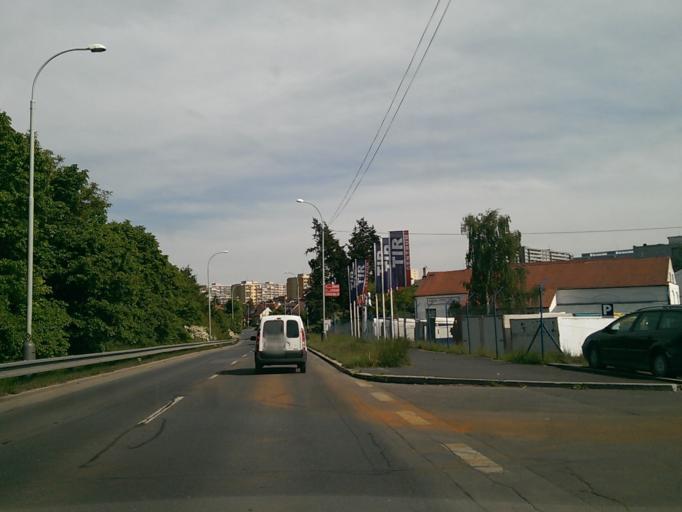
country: CZ
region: Central Bohemia
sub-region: Okres Praha-Zapad
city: Pruhonice
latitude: 50.0372
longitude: 14.5236
